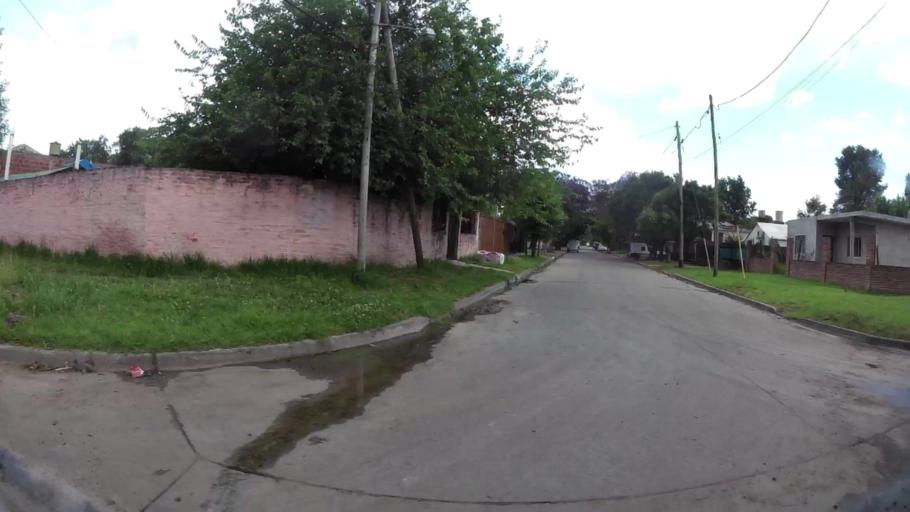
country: AR
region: Buenos Aires
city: Ituzaingo
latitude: -34.6386
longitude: -58.6827
